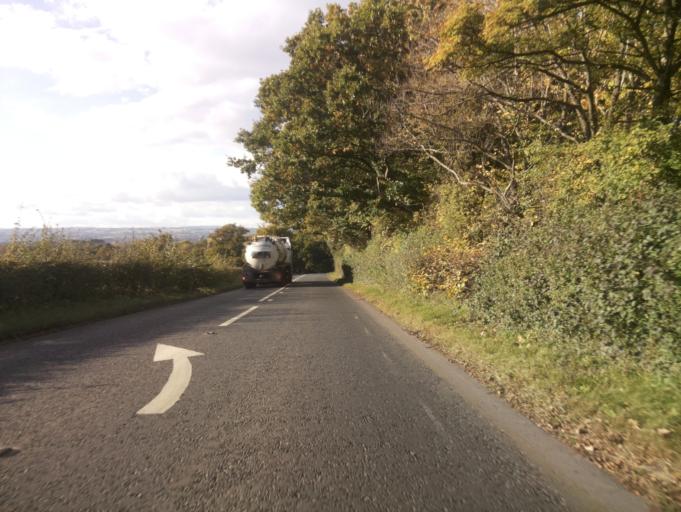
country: GB
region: England
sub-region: Herefordshire
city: Kinnersley
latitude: 52.1073
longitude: -2.9592
